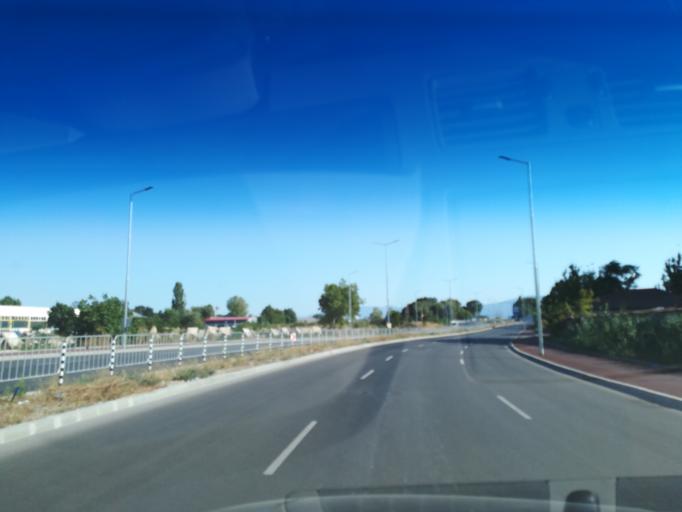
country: BG
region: Plovdiv
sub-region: Obshtina Plovdiv
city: Plovdiv
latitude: 42.1629
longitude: 24.7641
